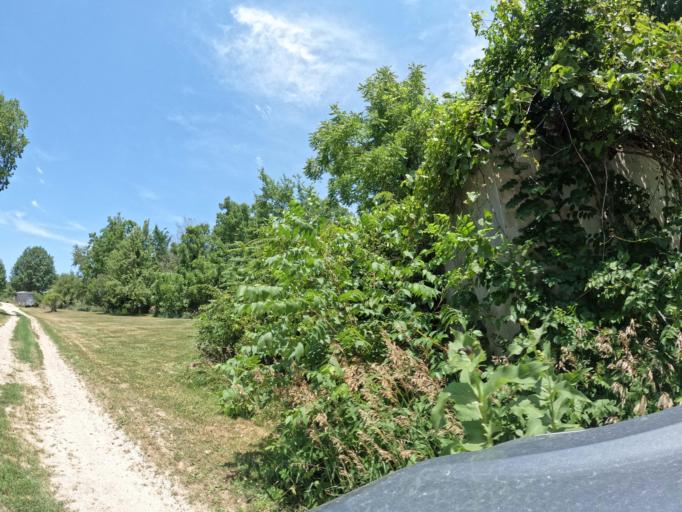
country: US
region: Iowa
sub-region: Henry County
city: Mount Pleasant
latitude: 40.9341
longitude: -91.6027
